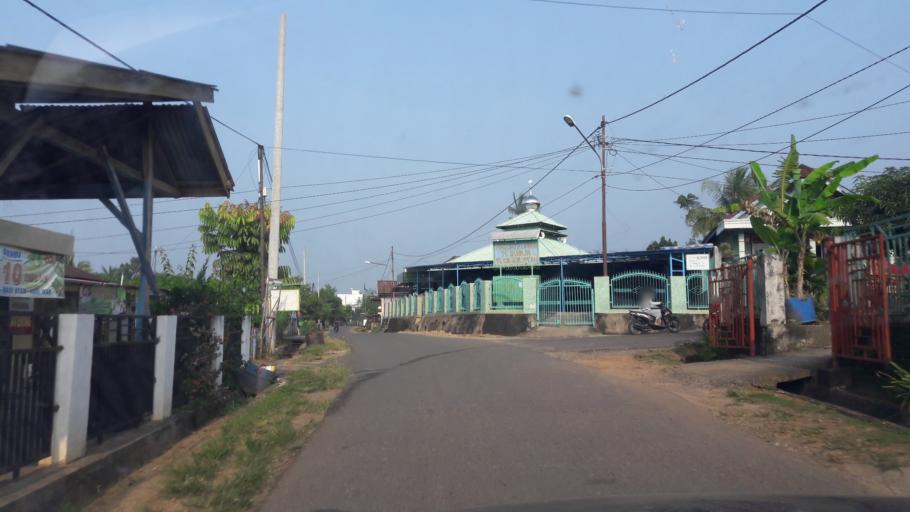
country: ID
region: South Sumatra
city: Gunungmegang Dalam
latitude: -3.2801
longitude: 103.8272
